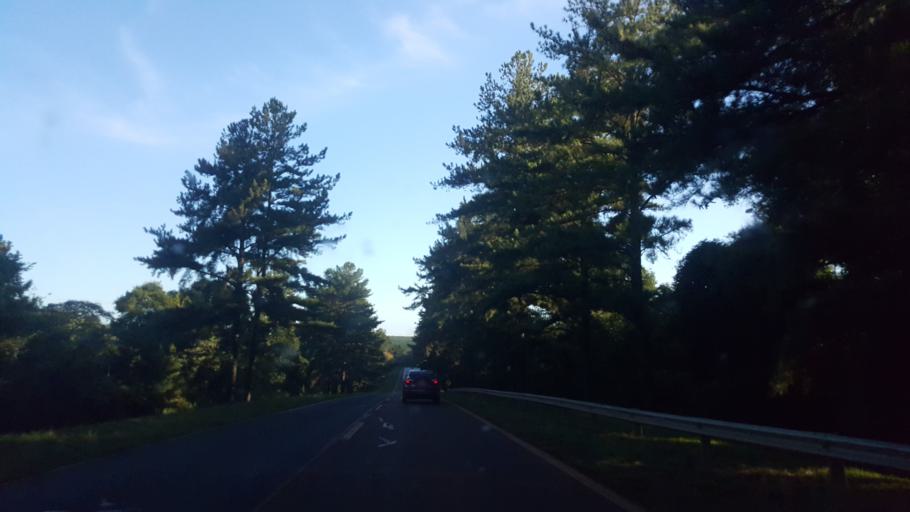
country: AR
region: Misiones
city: El Alcazar
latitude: -26.7514
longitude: -54.8840
